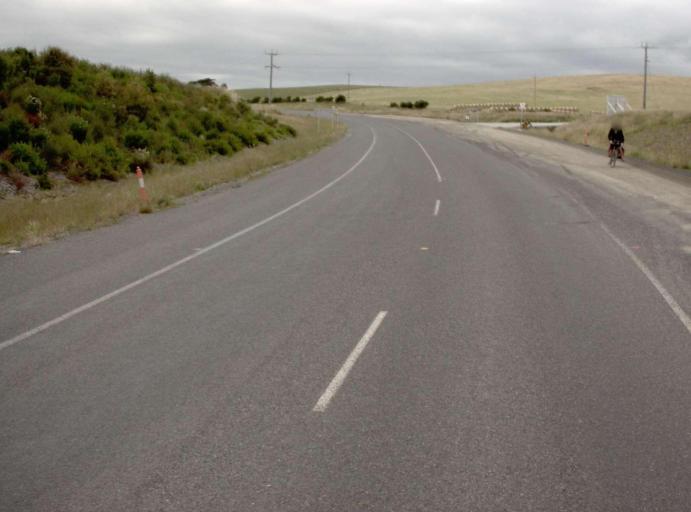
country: AU
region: Victoria
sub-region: Bass Coast
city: North Wonthaggi
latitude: -38.5250
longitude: 145.4336
